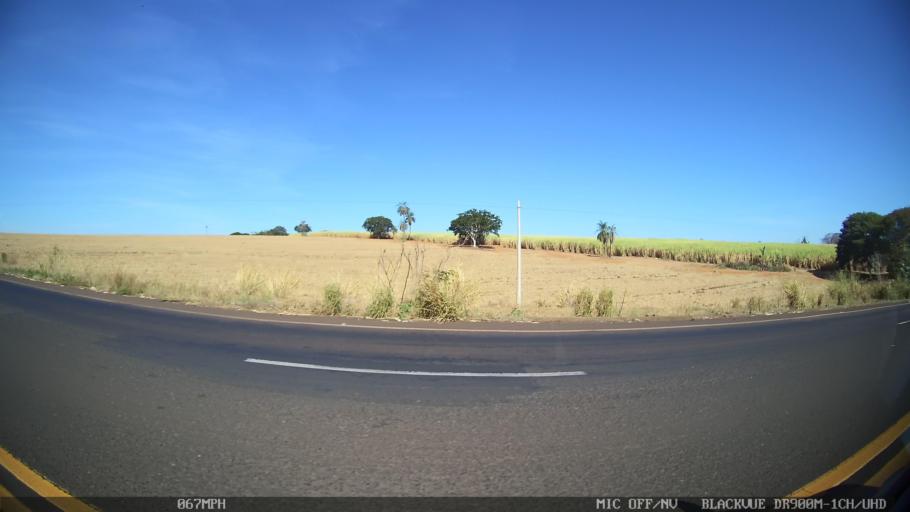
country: BR
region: Sao Paulo
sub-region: Barretos
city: Barretos
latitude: -20.6058
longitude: -48.7400
